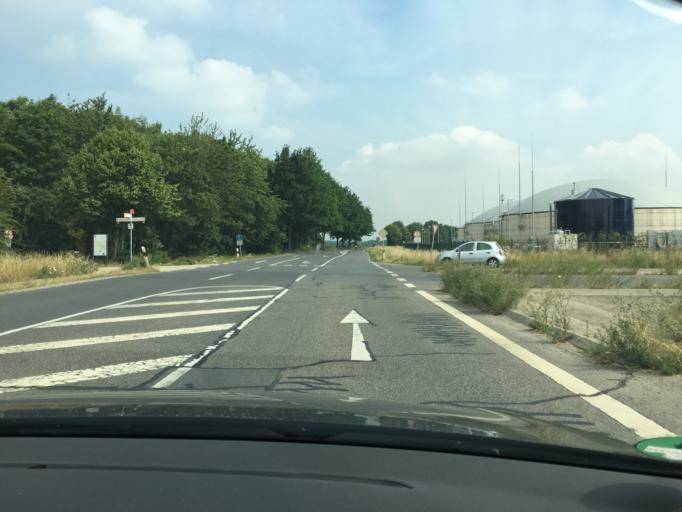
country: DE
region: North Rhine-Westphalia
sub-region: Regierungsbezirk Koln
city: Elsdorf
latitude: 50.9557
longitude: 6.5904
